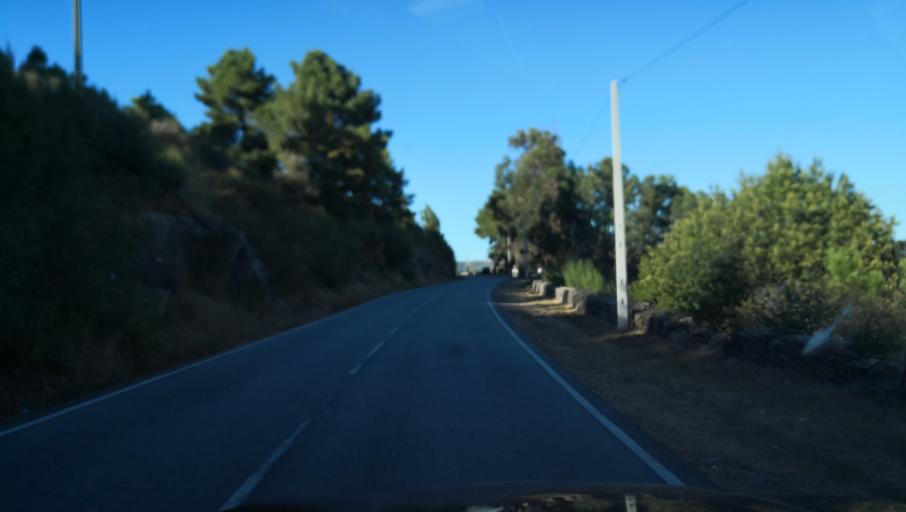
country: PT
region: Vila Real
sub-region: Sabrosa
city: Sabrosa
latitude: 41.2758
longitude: -7.5687
